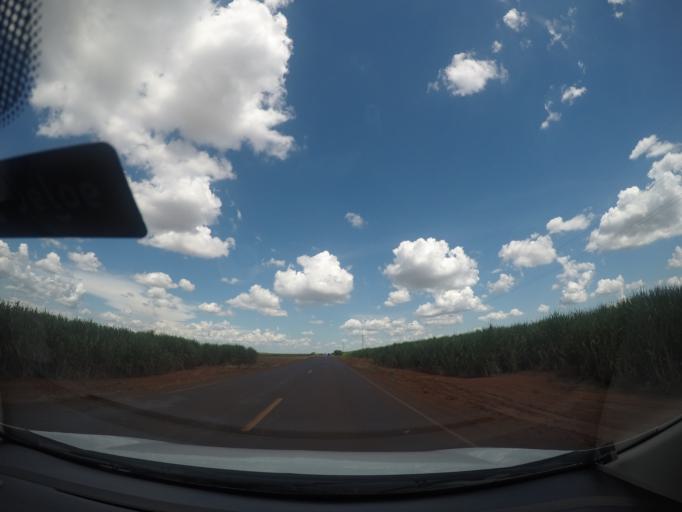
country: BR
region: Minas Gerais
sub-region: Frutal
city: Frutal
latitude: -19.8574
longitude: -48.7332
